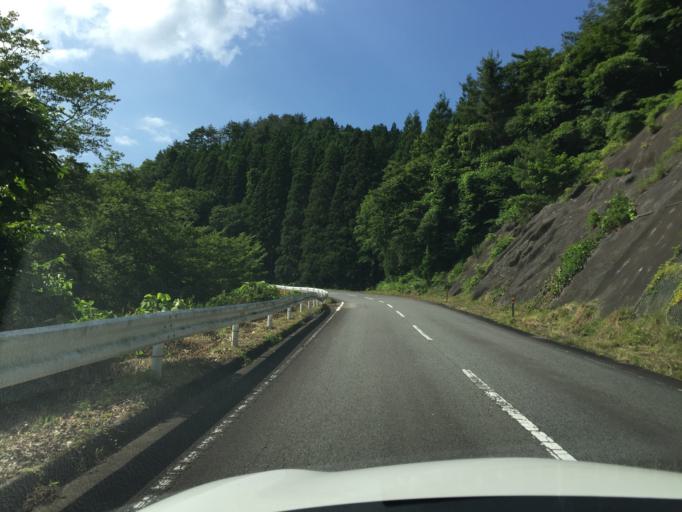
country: JP
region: Fukushima
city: Ishikawa
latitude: 37.1252
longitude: 140.6434
